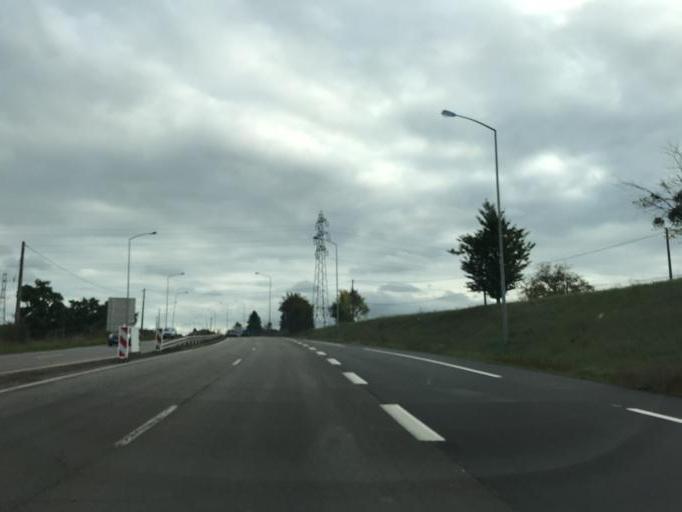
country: FR
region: Rhone-Alpes
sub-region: Departement de l'Ain
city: Viriat
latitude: 46.2319
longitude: 5.2006
